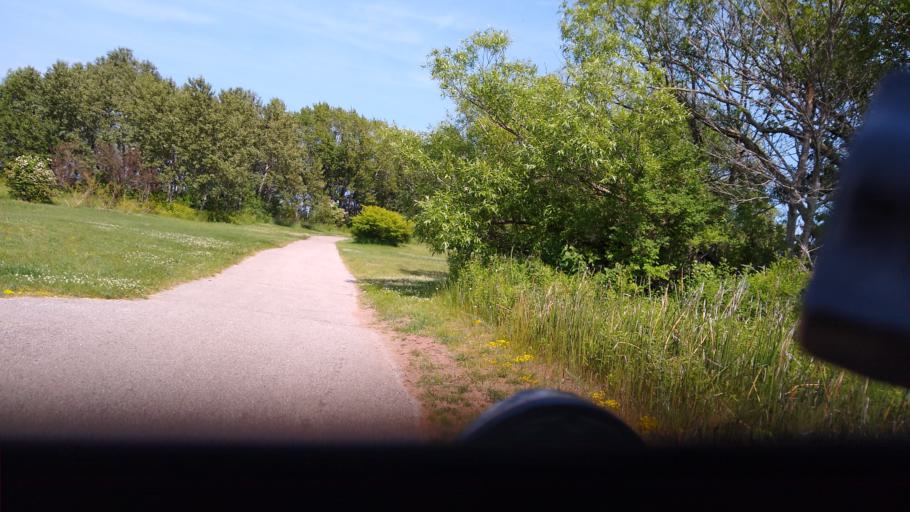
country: US
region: Michigan
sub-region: Delta County
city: Escanaba
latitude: 45.7420
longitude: -87.0403
